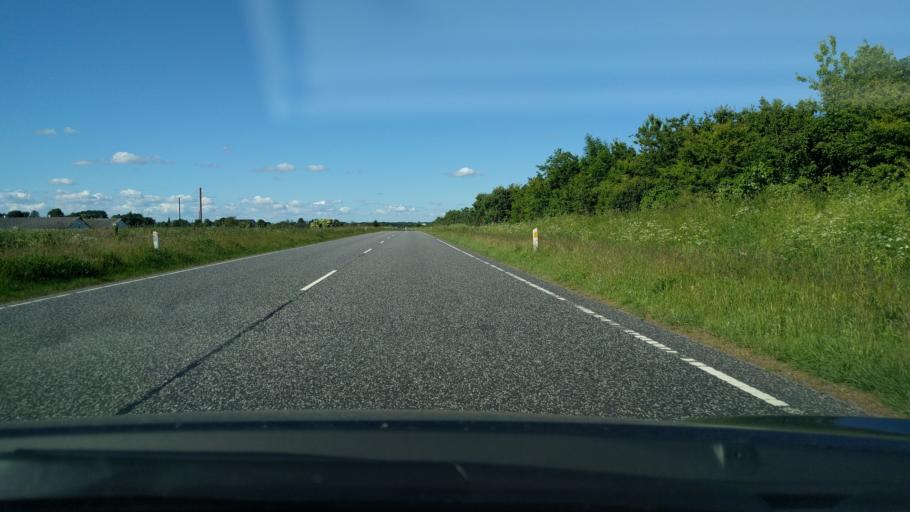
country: DK
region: North Denmark
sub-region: Vesthimmerland Kommune
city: Alestrup
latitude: 56.6064
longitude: 9.5033
